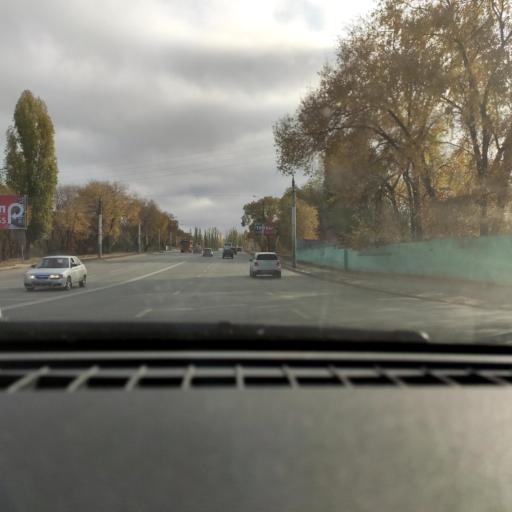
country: RU
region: Voronezj
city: Voronezh
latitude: 51.6240
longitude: 39.2330
